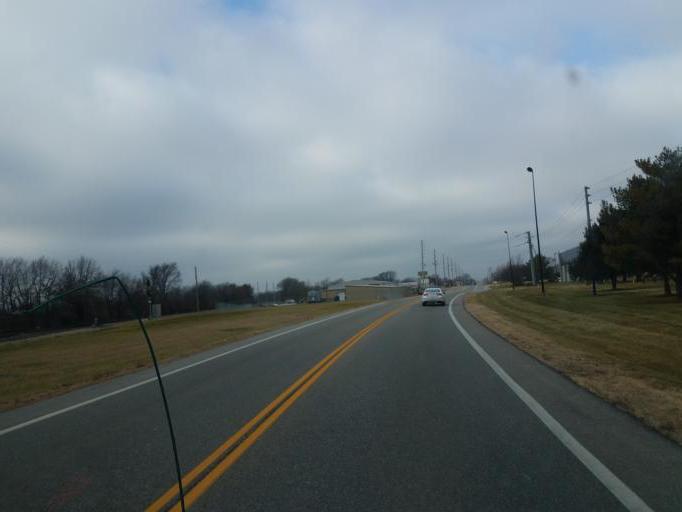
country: US
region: Missouri
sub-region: Greene County
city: Strafford
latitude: 37.2383
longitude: -93.2029
